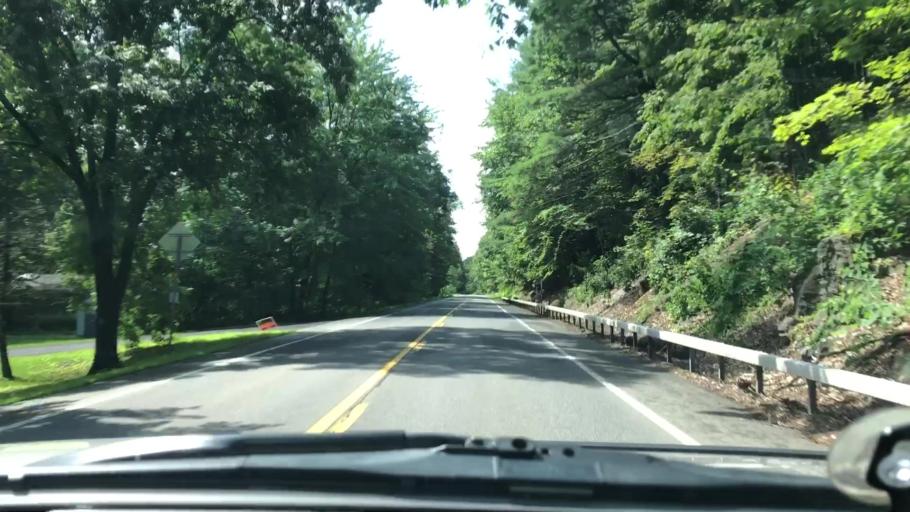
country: US
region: New York
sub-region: Greene County
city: Palenville
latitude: 42.2028
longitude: -73.9847
